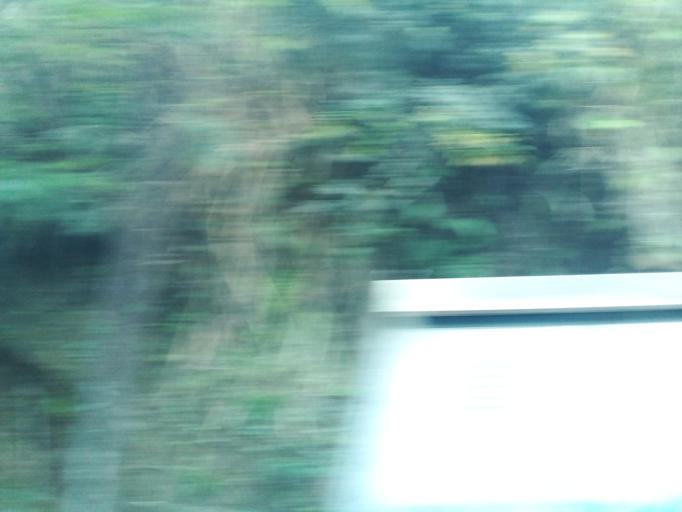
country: BR
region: Minas Gerais
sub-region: Joao Monlevade
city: Joao Monlevade
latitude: -19.8259
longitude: -43.1104
